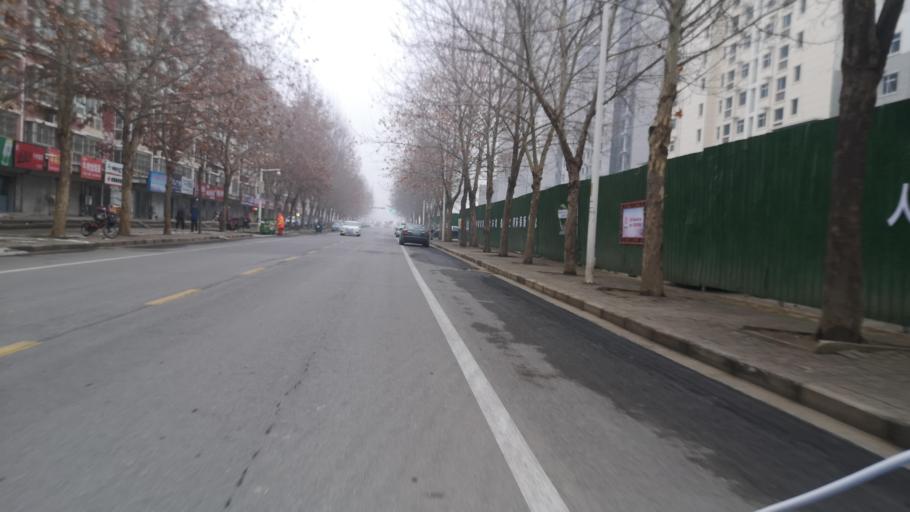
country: CN
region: Henan Sheng
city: Zhongyuanlu
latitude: 35.7639
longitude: 115.0810
